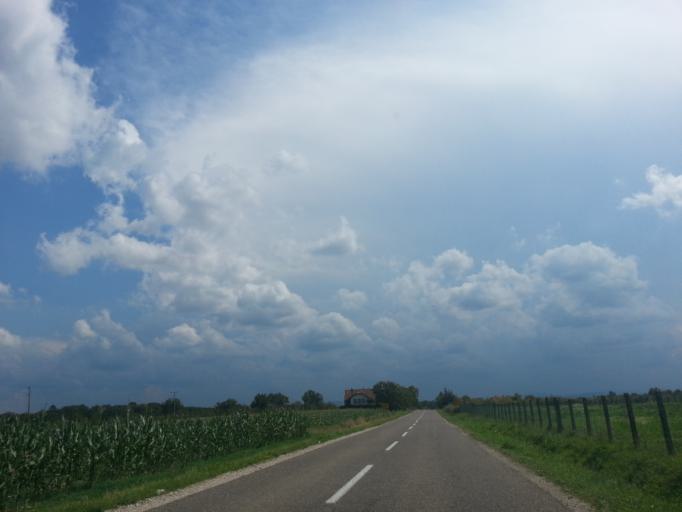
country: HR
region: Vukovarsko-Srijemska
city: Gunja
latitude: 44.8150
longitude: 18.8422
